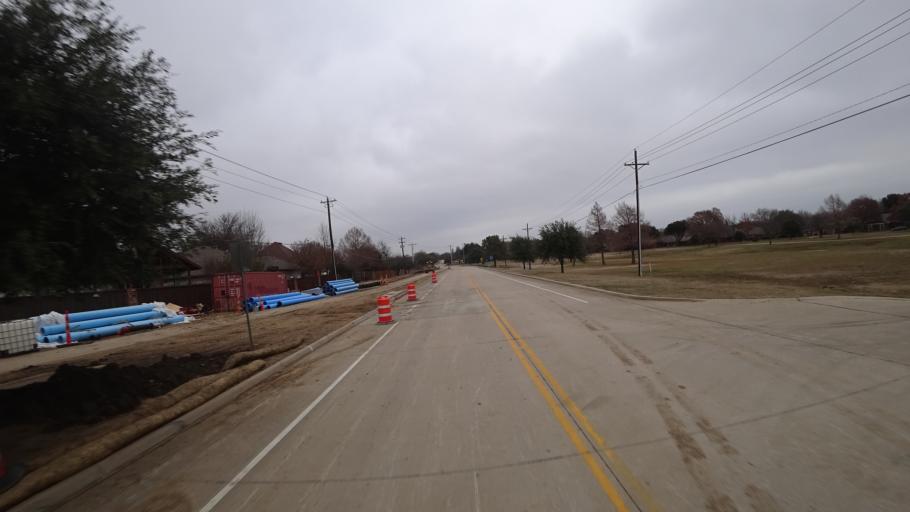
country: US
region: Texas
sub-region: Denton County
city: Highland Village
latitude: 33.0559
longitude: -97.0445
